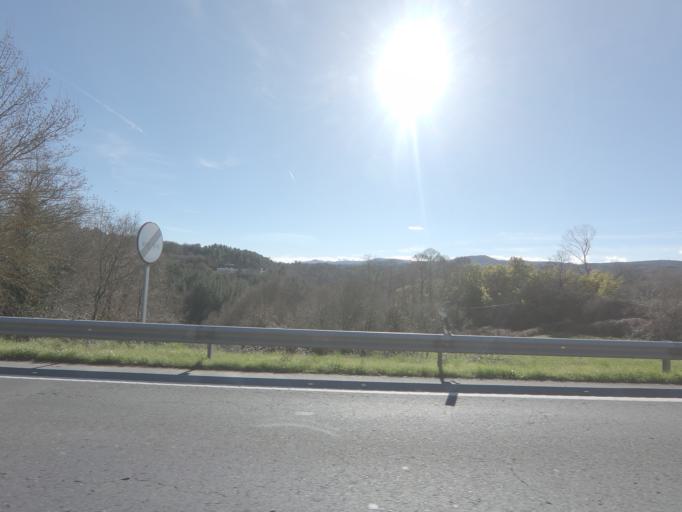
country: ES
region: Galicia
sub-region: Provincia de Pontevedra
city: Silleda
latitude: 42.6867
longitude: -8.2044
